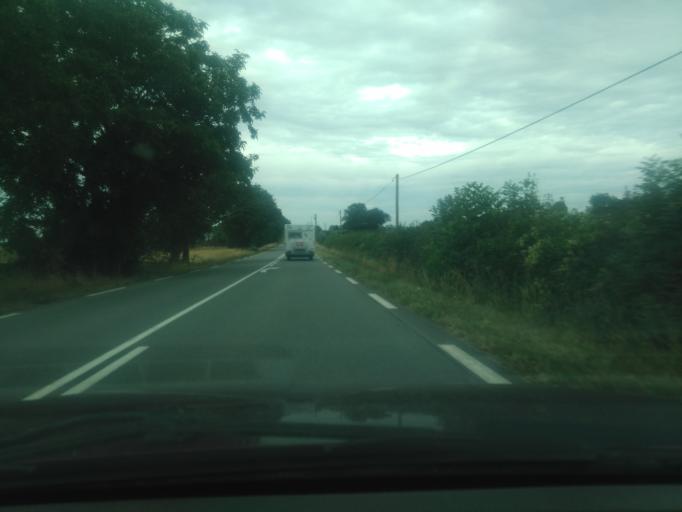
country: FR
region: Centre
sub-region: Departement du Cher
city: Sancoins
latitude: 46.7737
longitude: 2.8460
